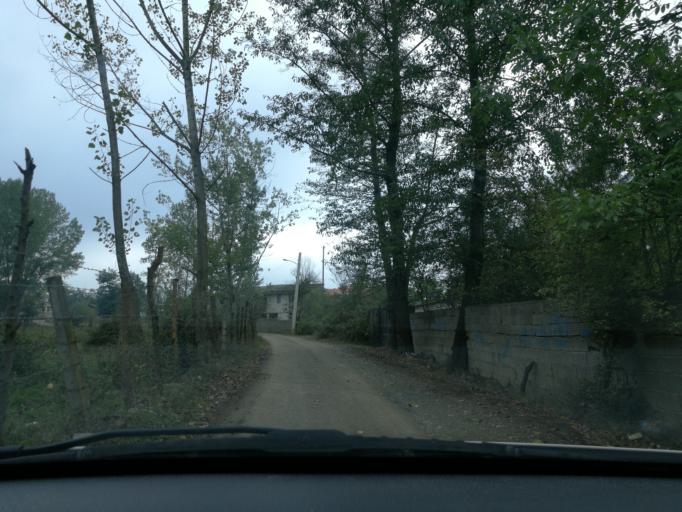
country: IR
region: Mazandaran
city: `Abbasabad
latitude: 36.5057
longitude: 51.1960
